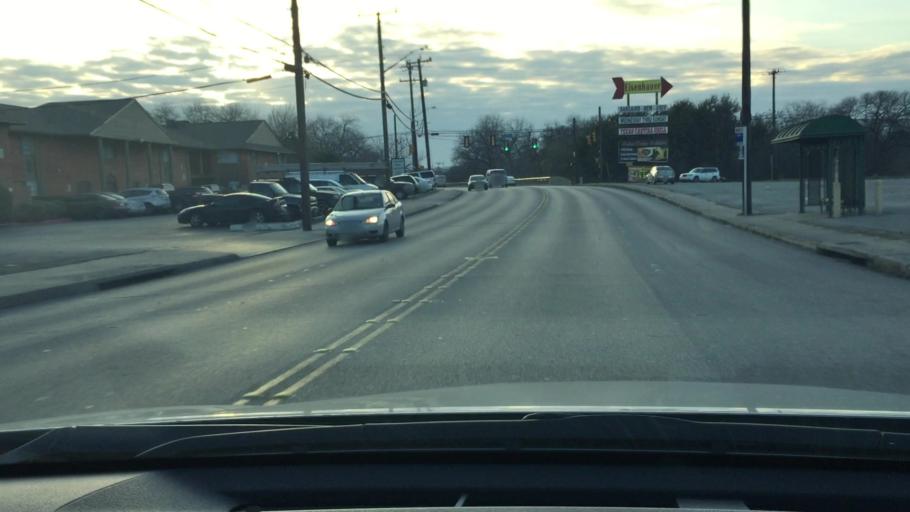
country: US
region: Texas
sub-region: Bexar County
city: Terrell Hills
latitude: 29.4966
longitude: -98.4196
